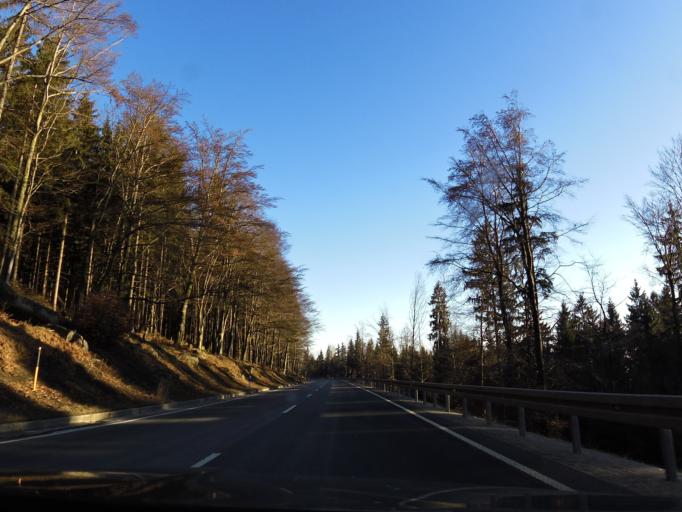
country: DE
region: Bavaria
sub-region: Upper Franconia
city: Fichtelberg
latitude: 50.0067
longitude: 11.8893
